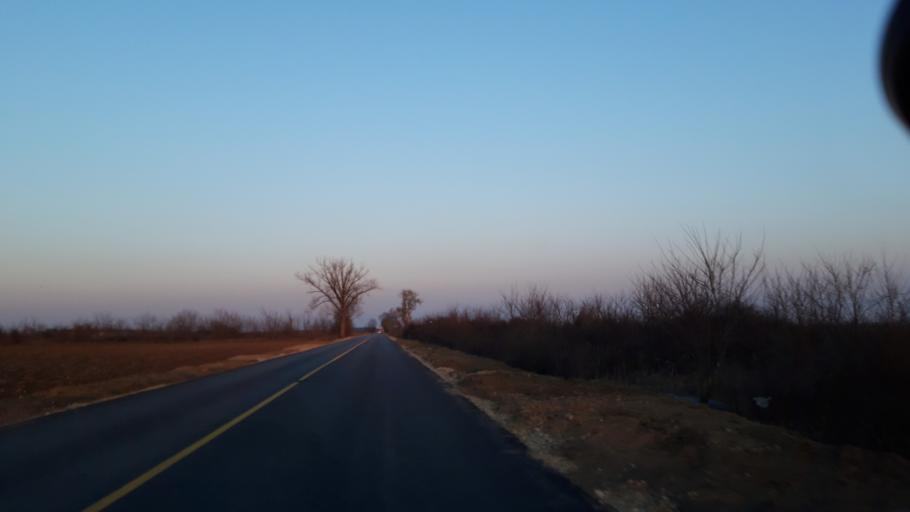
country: RS
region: Autonomna Pokrajina Vojvodina
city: Nova Pazova
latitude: 44.9865
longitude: 20.2300
